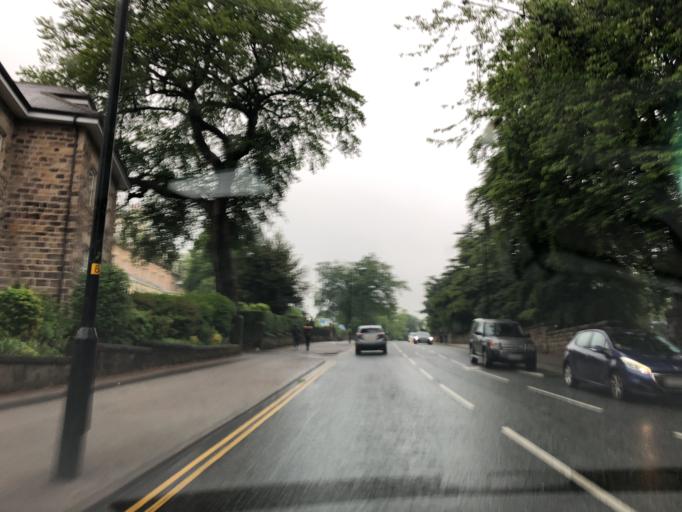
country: GB
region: England
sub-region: North Yorkshire
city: Harrogate
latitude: 53.9962
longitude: -1.5454
